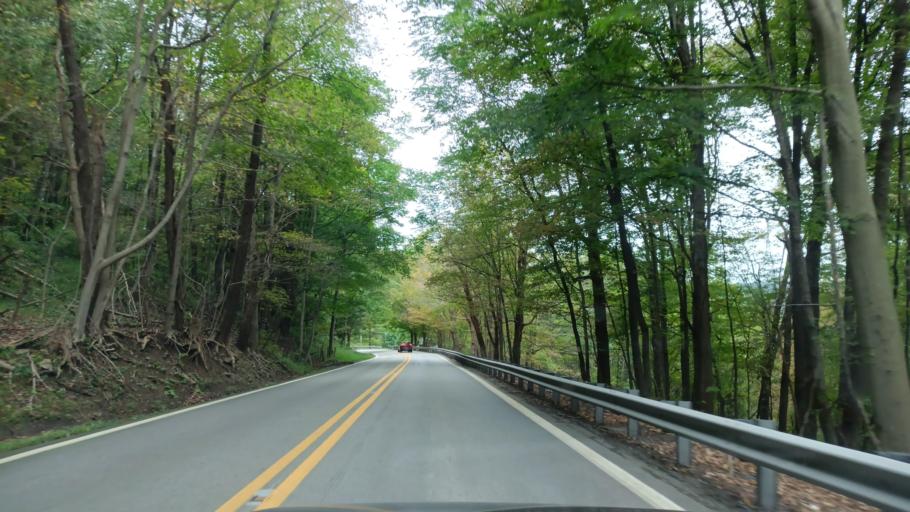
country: US
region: West Virginia
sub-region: Taylor County
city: Grafton
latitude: 39.3313
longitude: -79.9279
